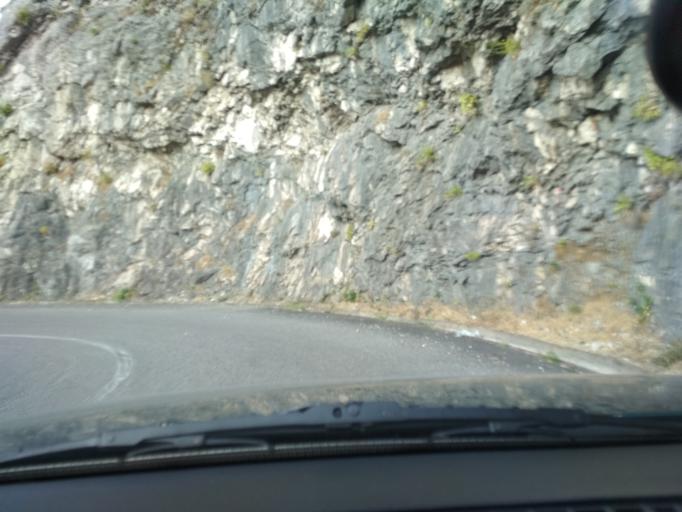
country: ME
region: Kotor
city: Kotor
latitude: 42.4100
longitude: 18.7702
